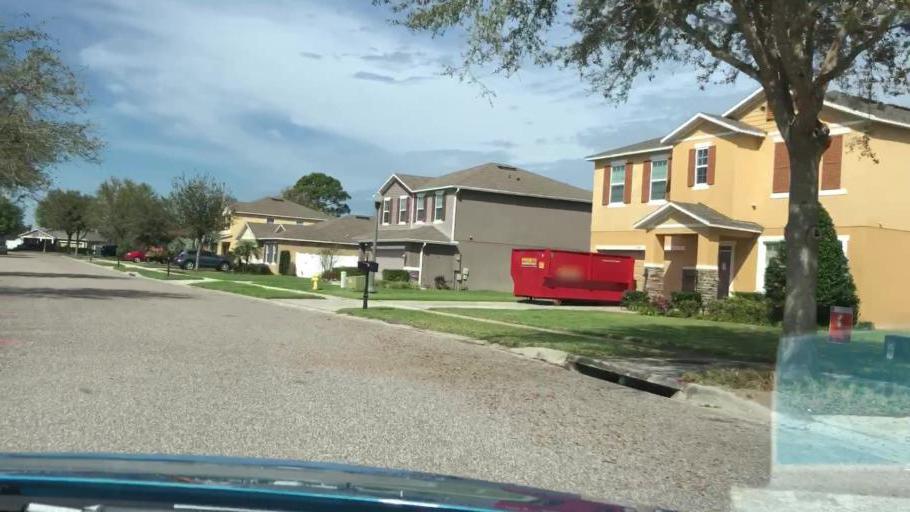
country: US
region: Florida
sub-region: Volusia County
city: Deltona
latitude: 28.8732
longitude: -81.2493
